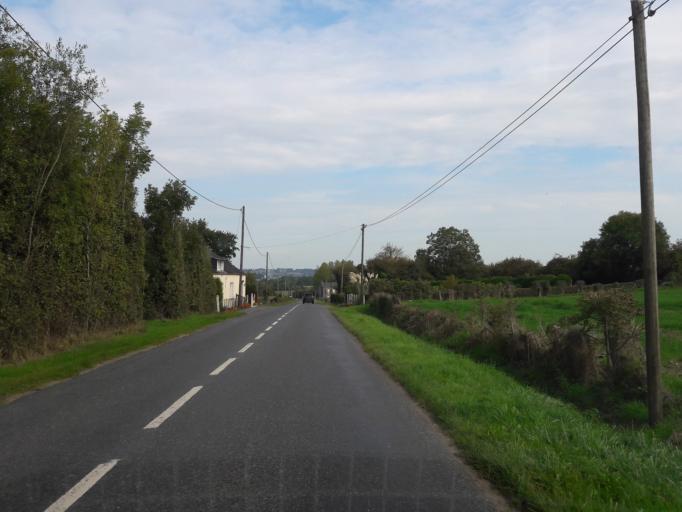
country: FR
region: Lower Normandy
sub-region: Departement du Calvados
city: Saint-Martin-des-Besaces
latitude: 49.0395
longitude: -0.8272
